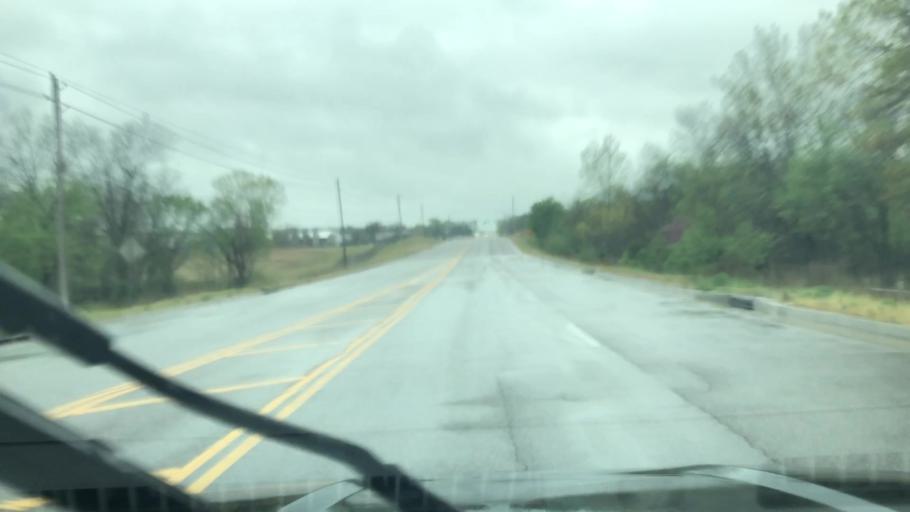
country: US
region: Oklahoma
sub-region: Tulsa County
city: Owasso
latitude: 36.2641
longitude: -95.9036
